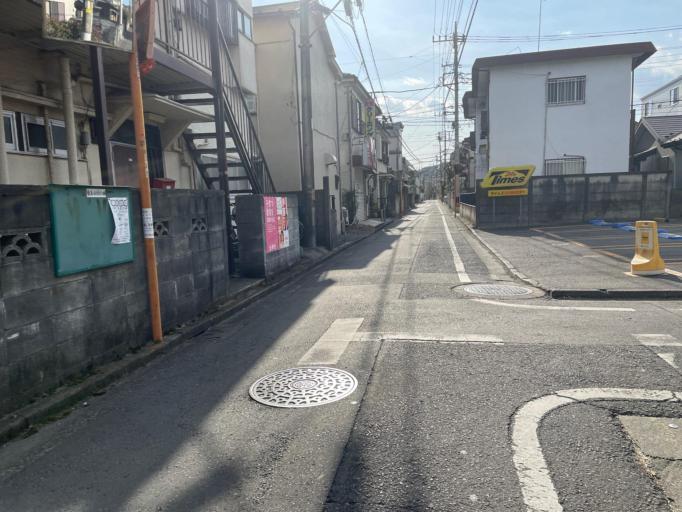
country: JP
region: Tokyo
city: Hino
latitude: 35.7051
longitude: 139.4224
